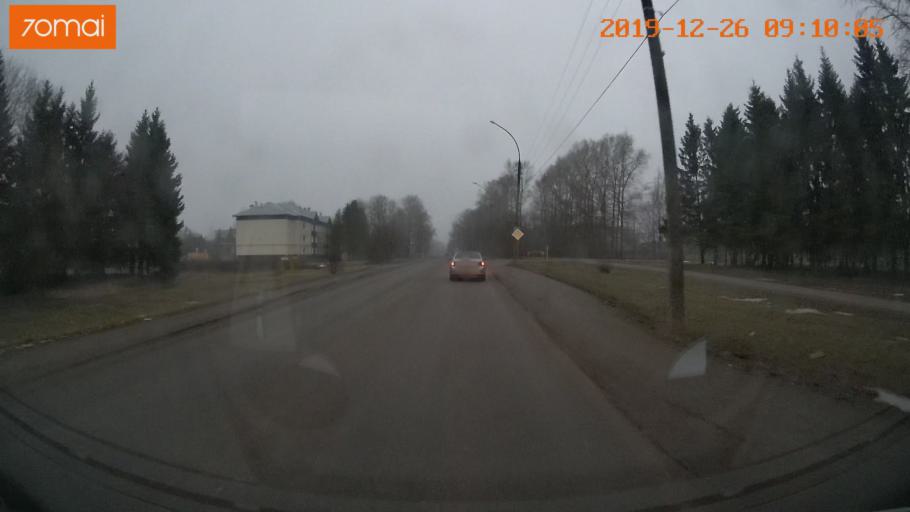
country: RU
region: Vologda
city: Gryazovets
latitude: 58.8688
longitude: 40.2528
